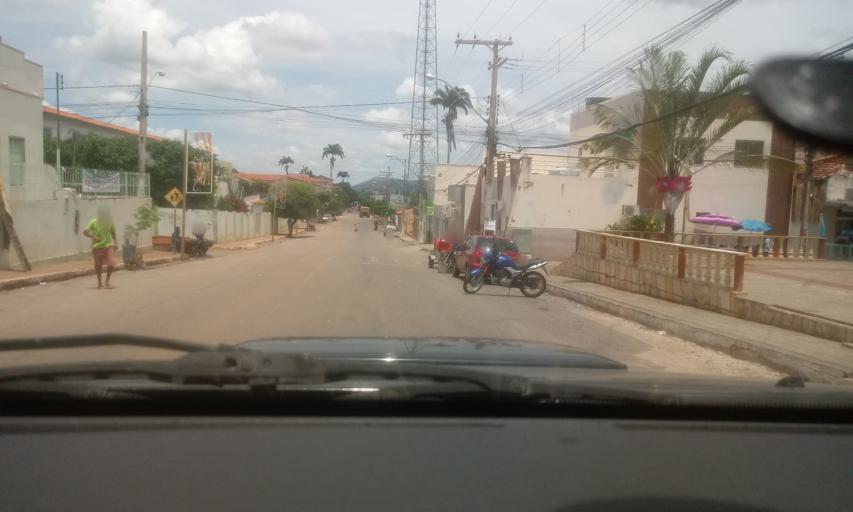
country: BR
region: Bahia
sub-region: Riacho De Santana
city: Riacho de Santana
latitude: -13.6095
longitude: -42.9367
